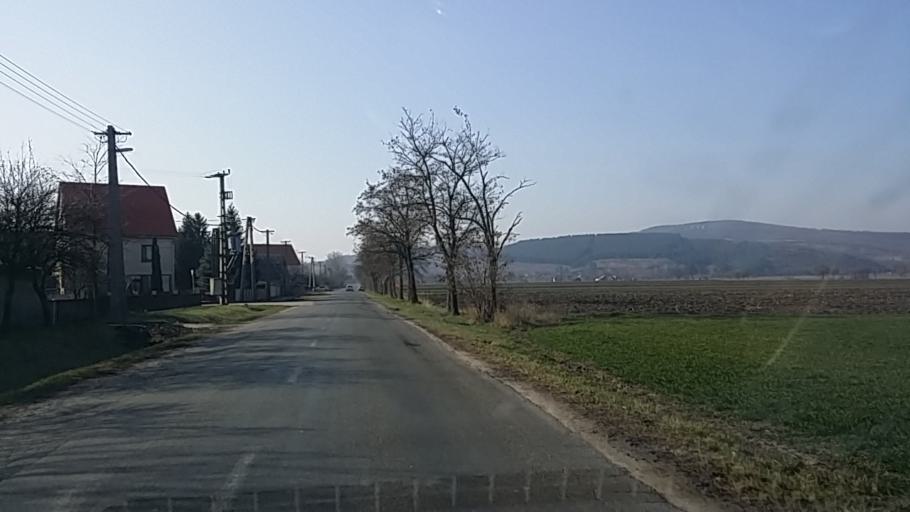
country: HU
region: Komarom-Esztergom
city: Tat
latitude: 47.7409
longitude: 18.6367
